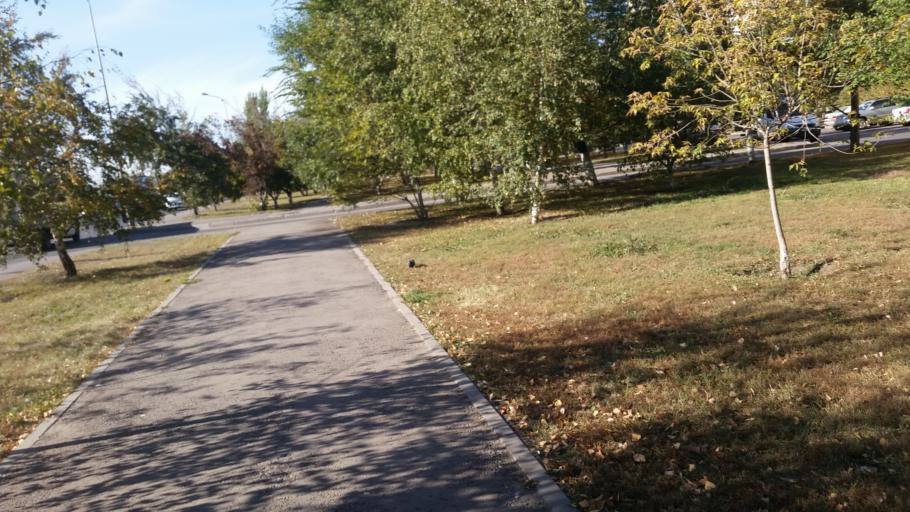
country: KZ
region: Astana Qalasy
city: Astana
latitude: 51.1624
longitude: 71.4694
